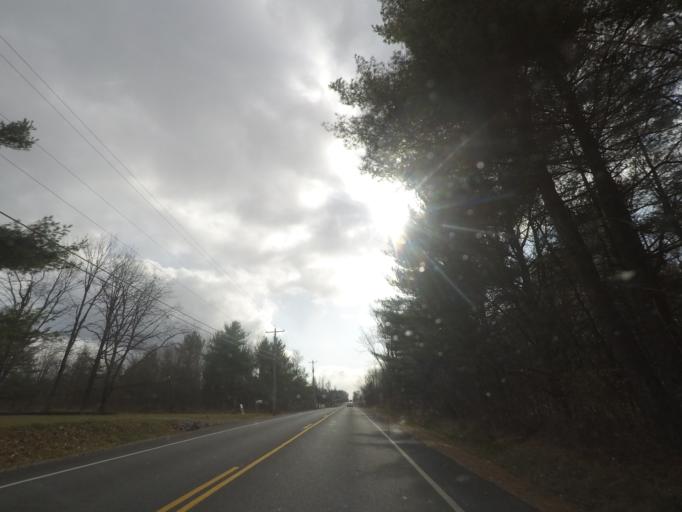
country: US
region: New York
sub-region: Saratoga County
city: Ballston Spa
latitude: 42.9669
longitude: -73.8303
